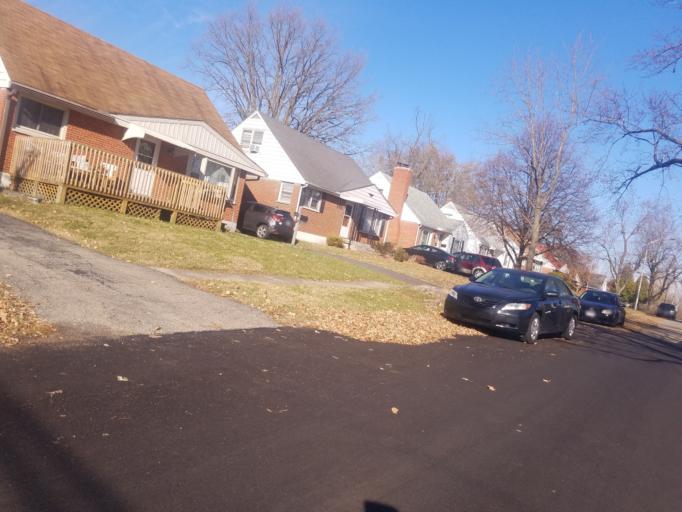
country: US
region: Ohio
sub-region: Montgomery County
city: Kettering
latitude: 39.7072
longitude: -84.1532
